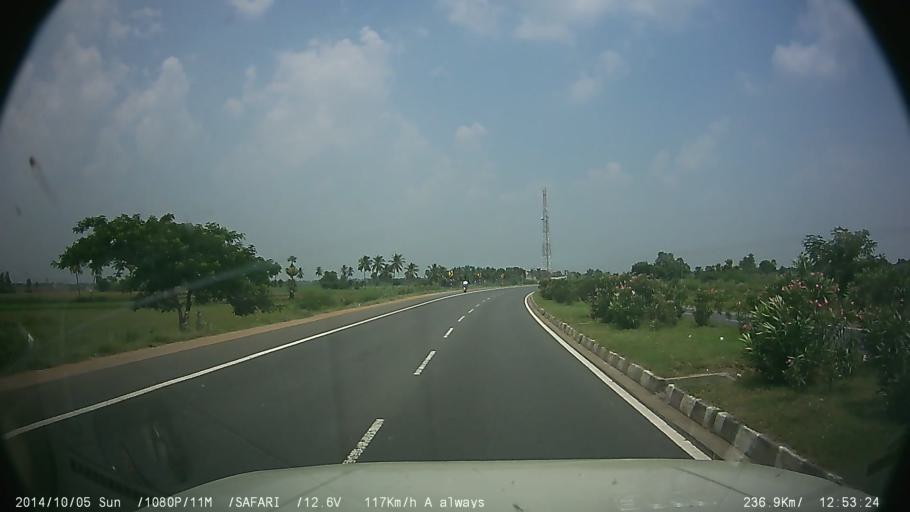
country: IN
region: Tamil Nadu
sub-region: Cuddalore
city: Panruti
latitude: 11.7467
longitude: 79.3681
